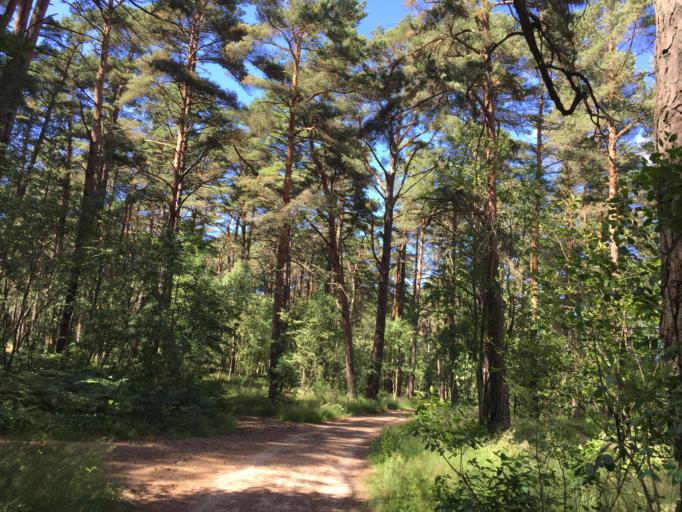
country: LV
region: Ventspils
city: Ventspils
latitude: 57.4470
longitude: 21.6302
